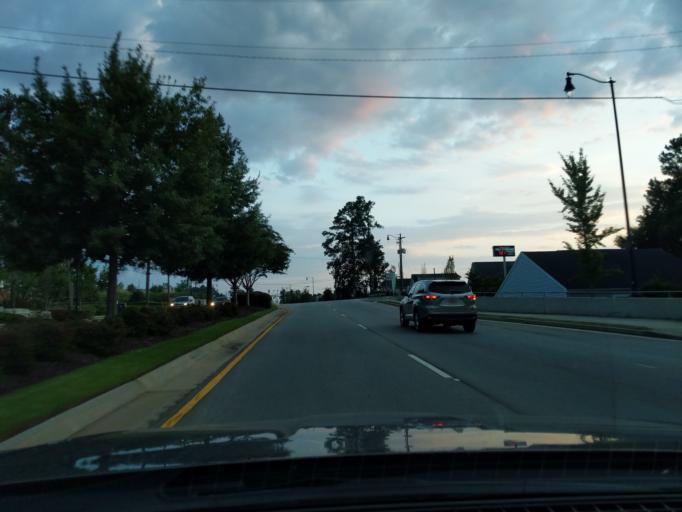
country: US
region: Georgia
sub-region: Columbia County
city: Martinez
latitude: 33.5136
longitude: -82.0267
